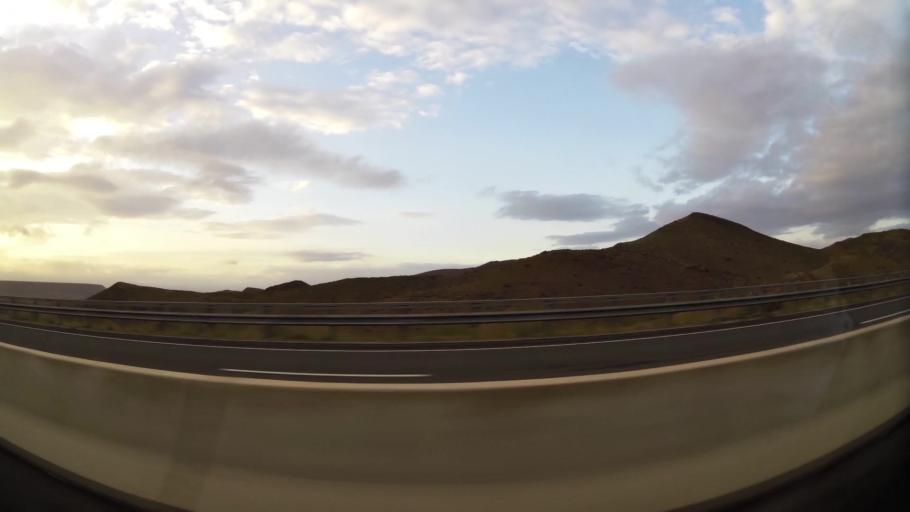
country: MA
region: Oriental
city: Taourirt
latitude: 34.4690
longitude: -3.0251
